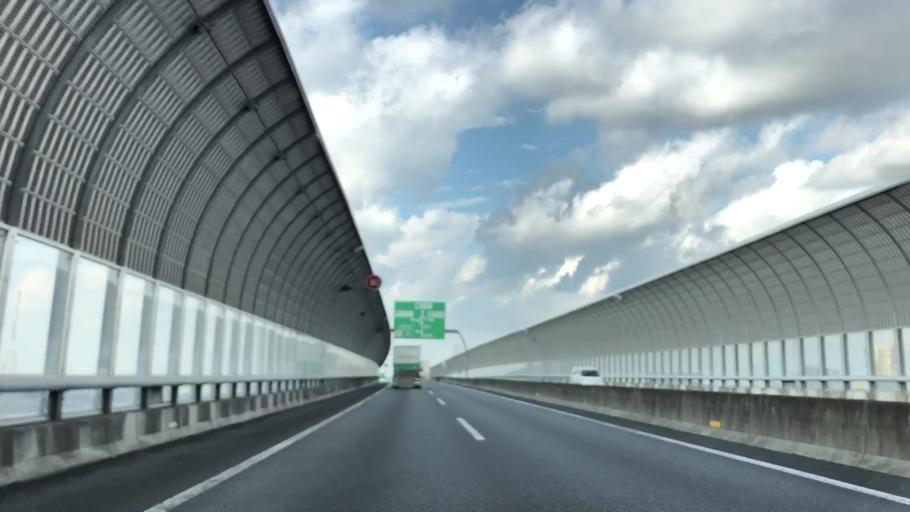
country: JP
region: Saitama
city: Yashio-shi
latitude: 35.8164
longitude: 139.8746
